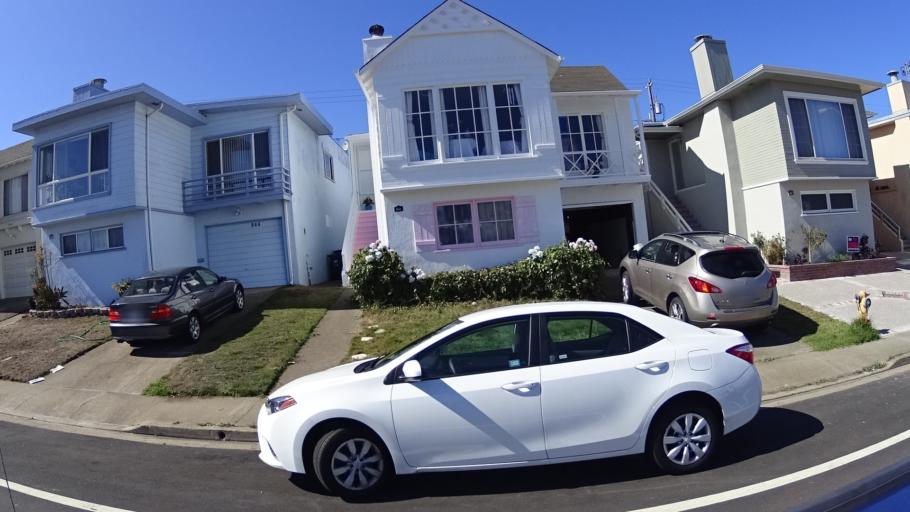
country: US
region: California
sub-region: San Mateo County
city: Broadmoor
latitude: 37.6878
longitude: -122.4880
